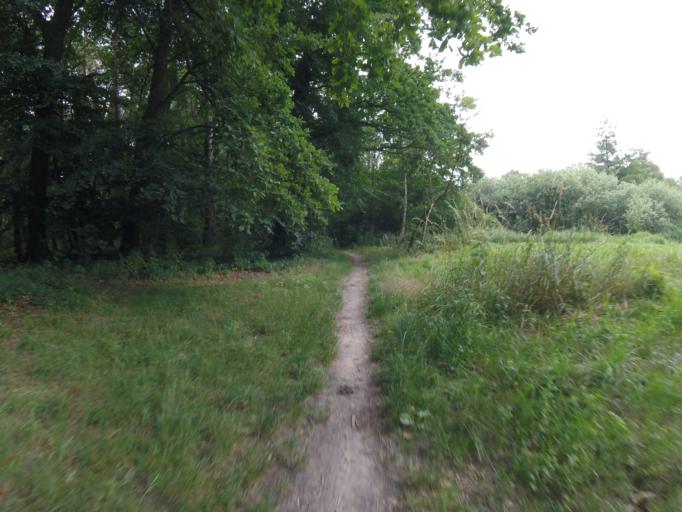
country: DE
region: Brandenburg
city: Konigs Wusterhausen
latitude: 52.2886
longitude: 13.6405
